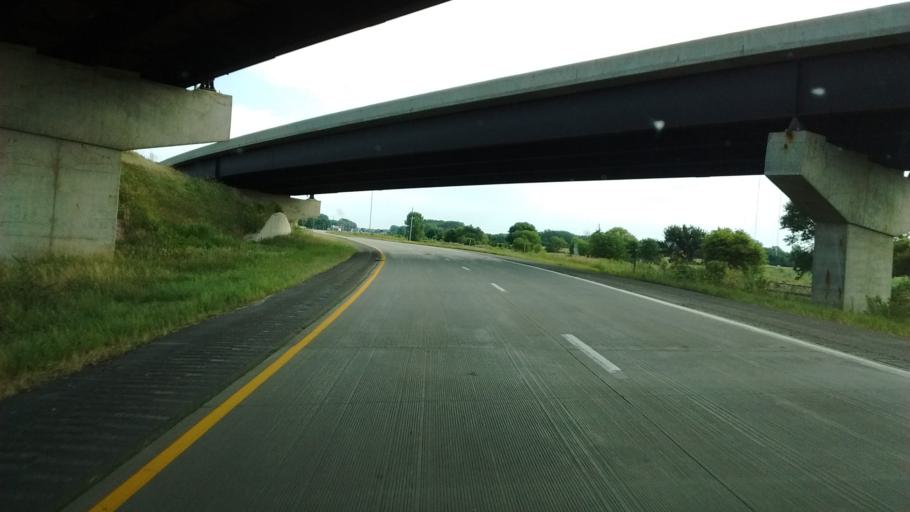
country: US
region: Iowa
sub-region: Woodbury County
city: Sioux City
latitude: 42.5533
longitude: -96.3417
